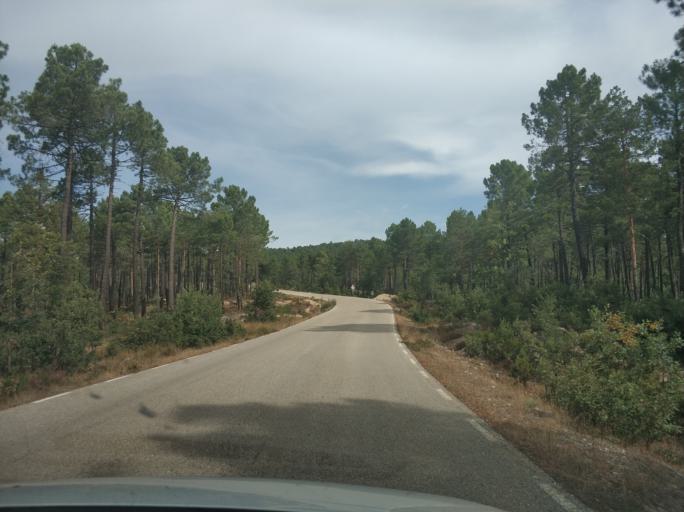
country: ES
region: Castille and Leon
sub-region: Provincia de Soria
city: Duruelo de la Sierra
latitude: 41.8841
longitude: -2.9374
